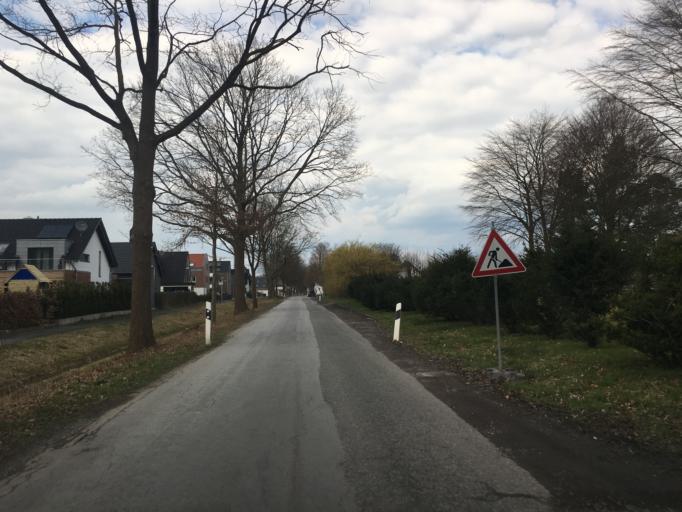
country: DE
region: North Rhine-Westphalia
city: Ludinghausen
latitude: 51.7780
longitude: 7.4646
